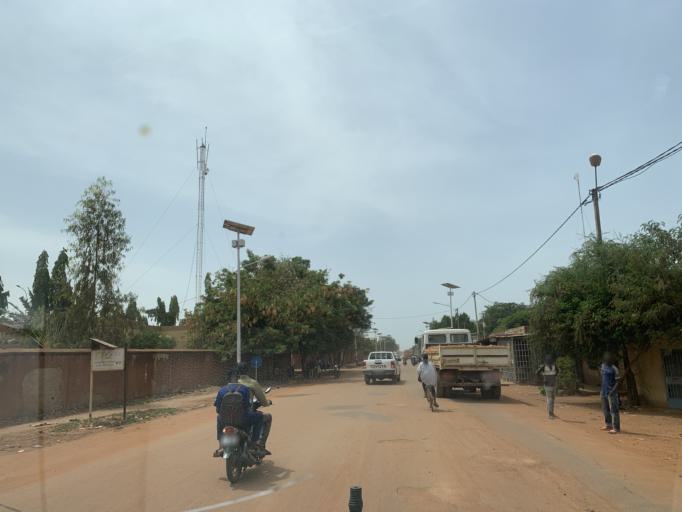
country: BF
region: Centre
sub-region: Kadiogo Province
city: Ouagadougou
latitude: 12.3352
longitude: -1.4976
